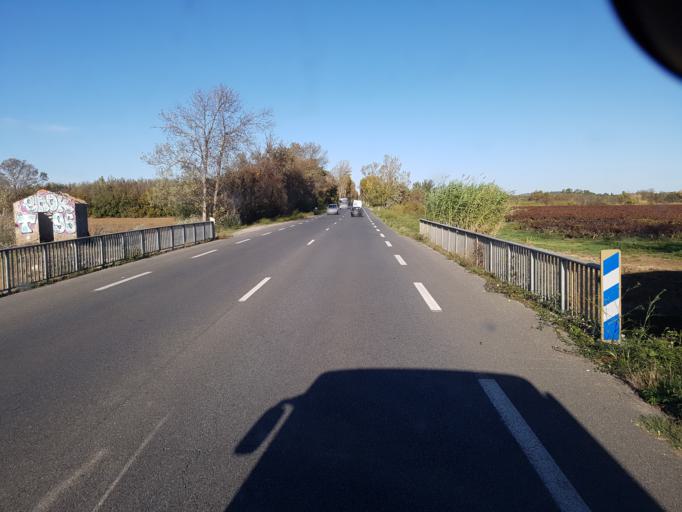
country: FR
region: Languedoc-Roussillon
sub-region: Departement de l'Aude
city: Coursan
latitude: 43.2130
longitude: 3.0315
